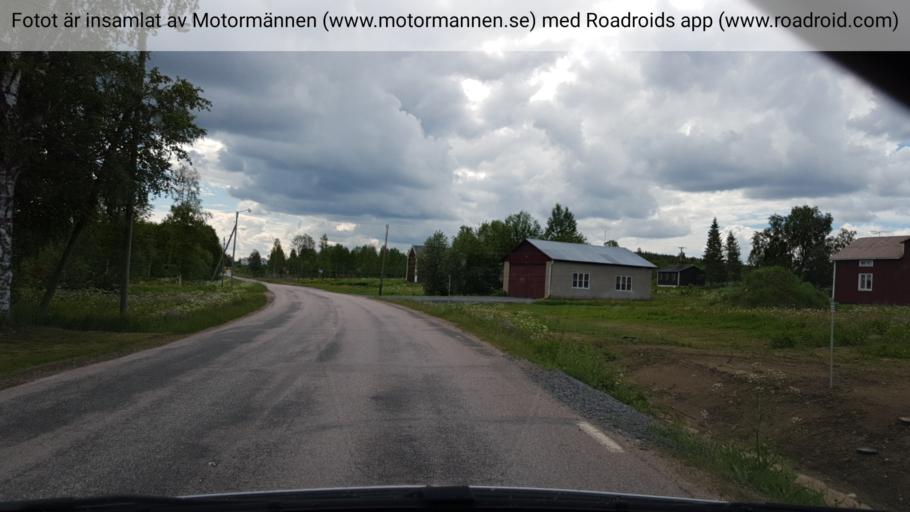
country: FI
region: Lapland
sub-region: Torniolaakso
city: Ylitornio
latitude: 66.2209
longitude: 23.6927
